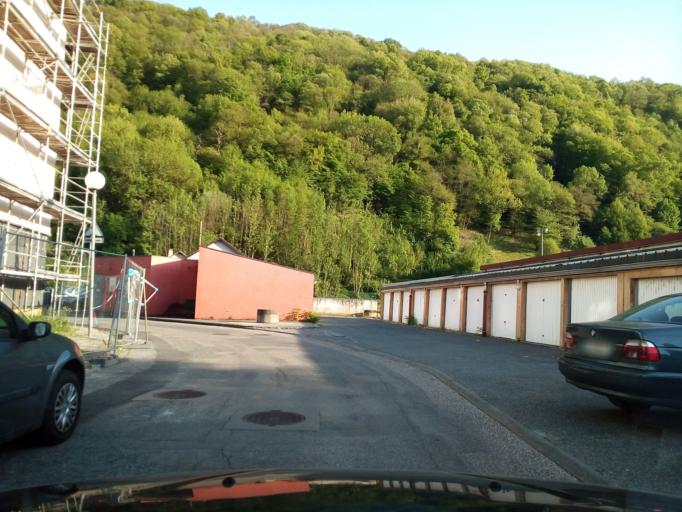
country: FR
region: Rhone-Alpes
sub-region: Departement de l'Isere
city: Gieres
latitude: 45.1872
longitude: 5.8077
